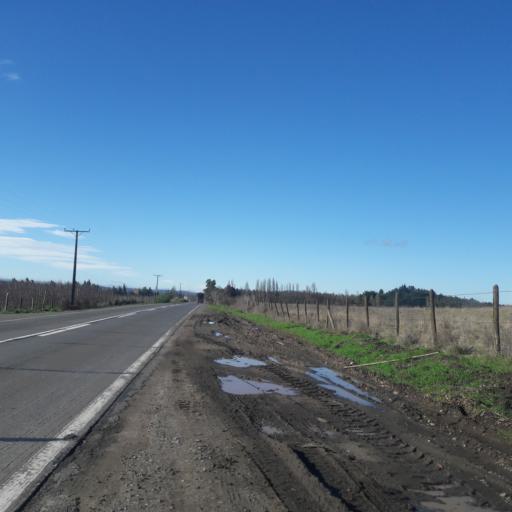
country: CL
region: Araucania
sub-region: Provincia de Malleco
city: Angol
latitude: -37.7467
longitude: -72.5949
